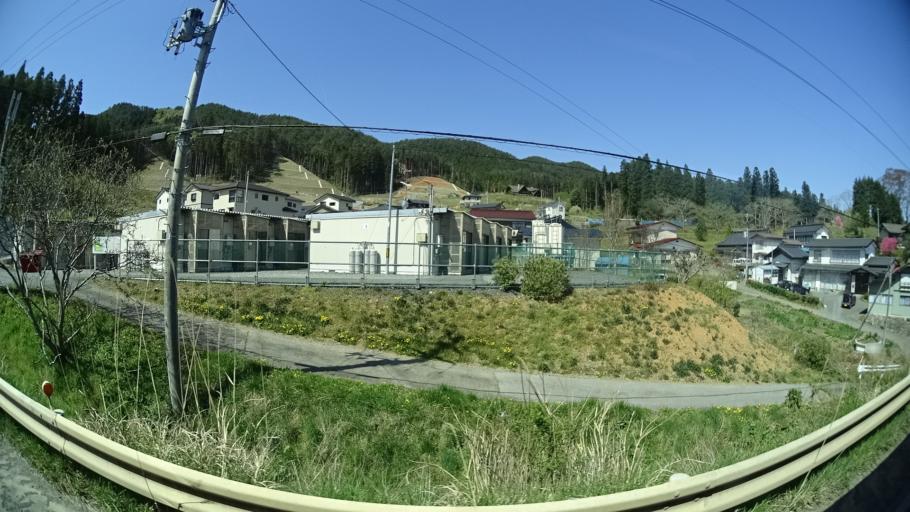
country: JP
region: Iwate
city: Ofunato
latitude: 38.9806
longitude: 141.6215
